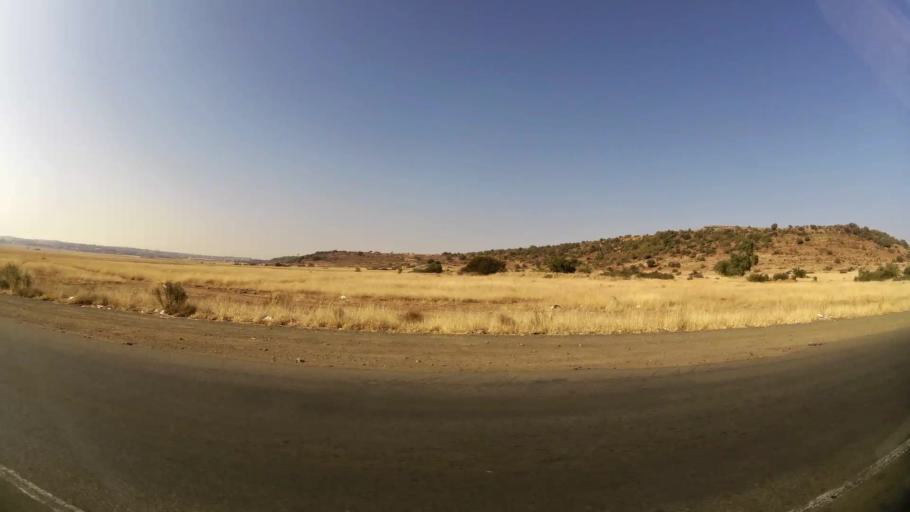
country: ZA
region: Orange Free State
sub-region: Mangaung Metropolitan Municipality
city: Bloemfontein
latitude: -29.1729
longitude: 26.1992
